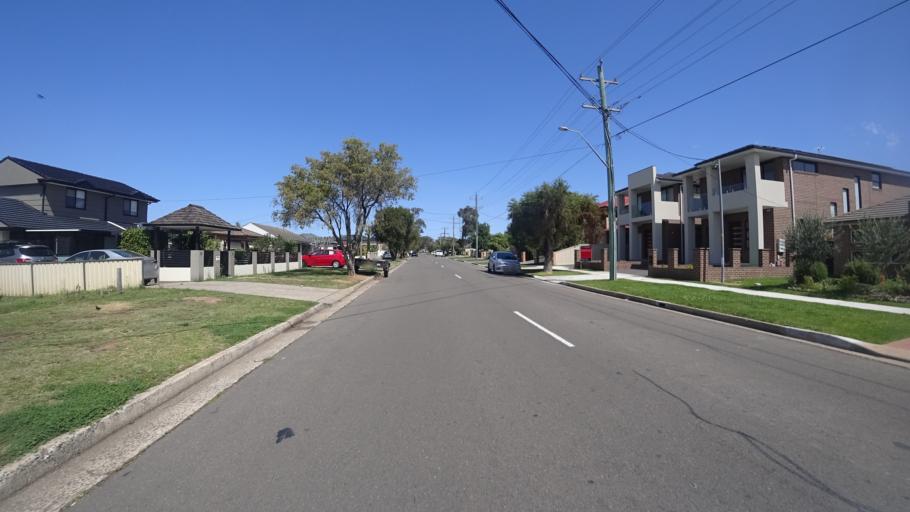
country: AU
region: New South Wales
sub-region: Liverpool
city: Miller
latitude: -33.9360
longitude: 150.8994
